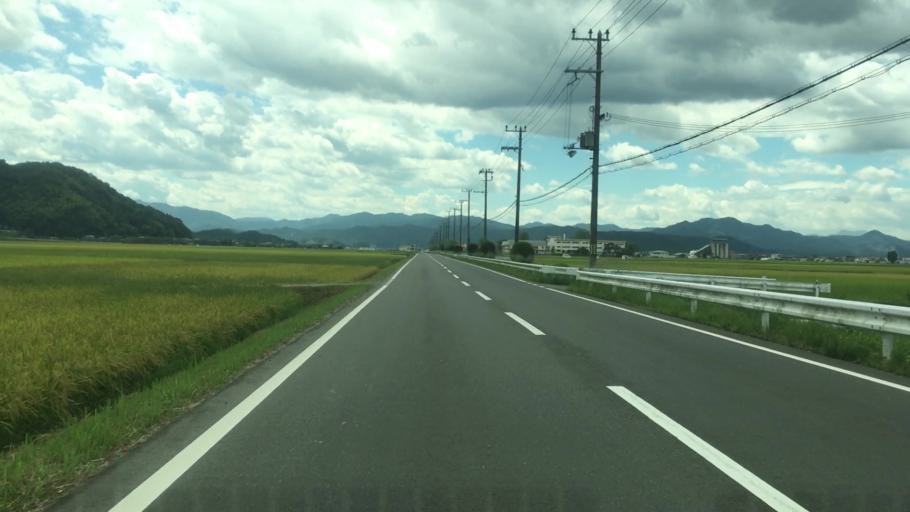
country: JP
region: Hyogo
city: Toyooka
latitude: 35.5374
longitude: 134.8397
